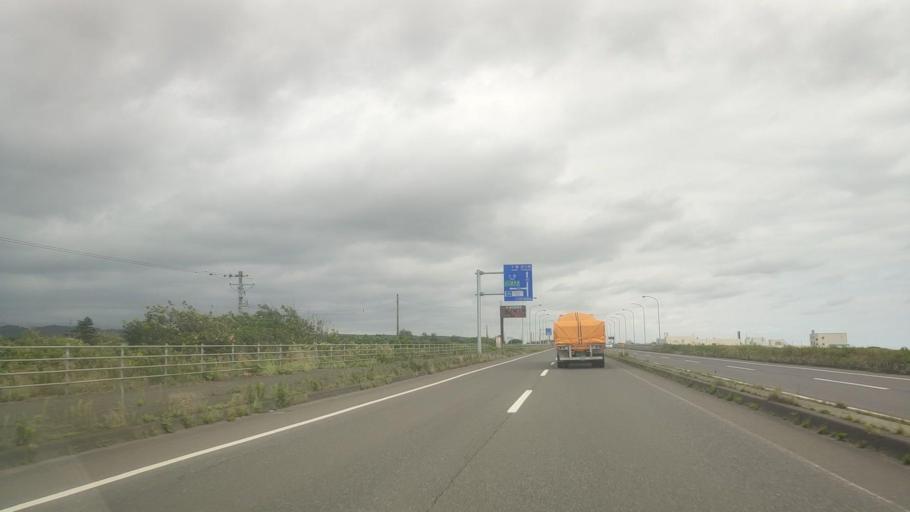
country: JP
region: Hokkaido
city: Shiraoi
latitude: 42.5414
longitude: 141.3436
